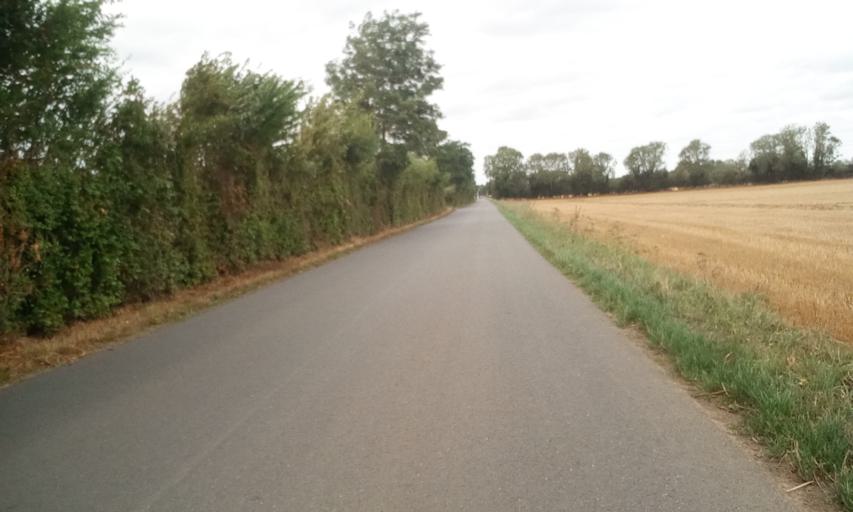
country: FR
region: Lower Normandy
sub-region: Departement du Calvados
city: Fontaine-Etoupefour
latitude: 49.1315
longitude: -0.4645
